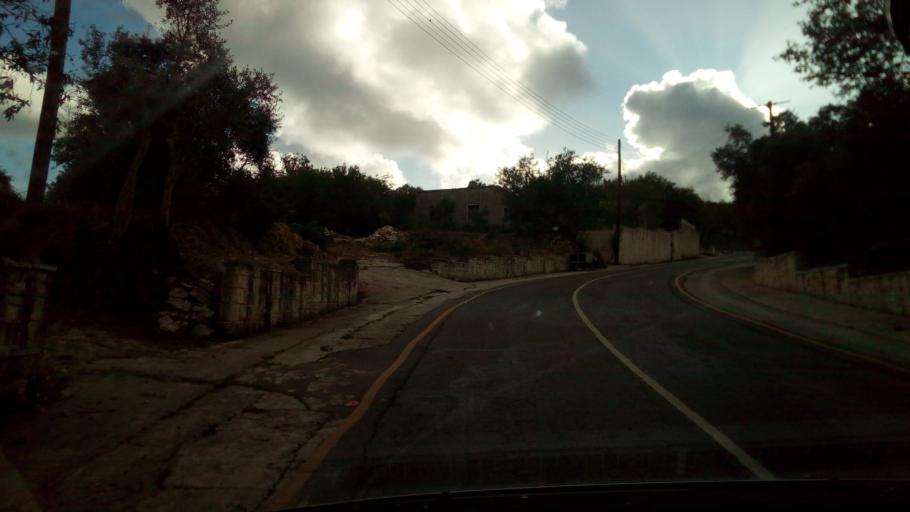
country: CY
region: Pafos
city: Mesogi
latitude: 34.8578
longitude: 32.5088
